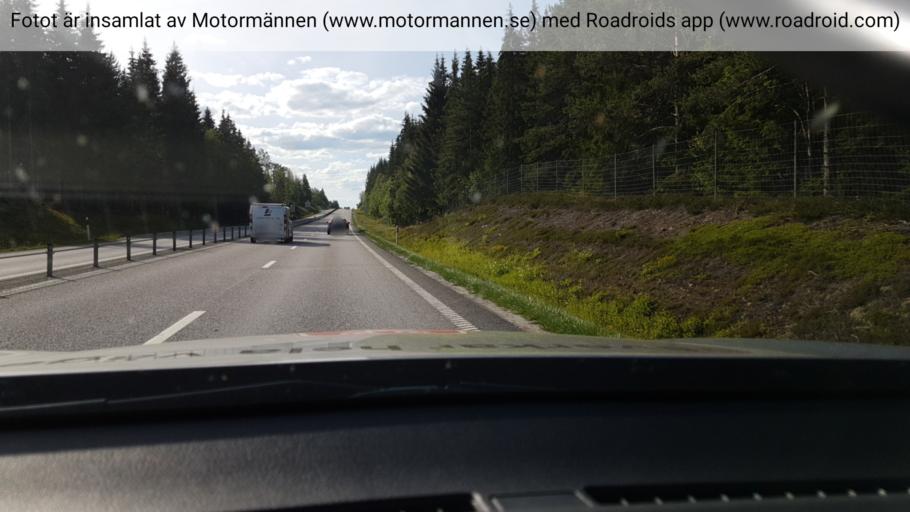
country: SE
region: Vaestra Goetaland
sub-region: Ulricehamns Kommun
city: Ulricehamn
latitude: 57.7828
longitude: 13.6504
